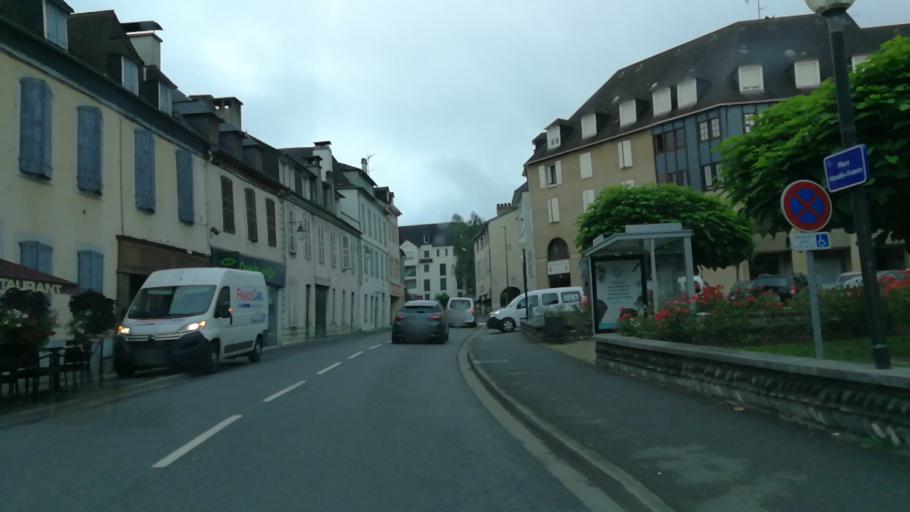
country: FR
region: Aquitaine
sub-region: Departement des Pyrenees-Atlantiques
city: Oloron-Sainte-Marie
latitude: 43.1890
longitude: -0.6113
